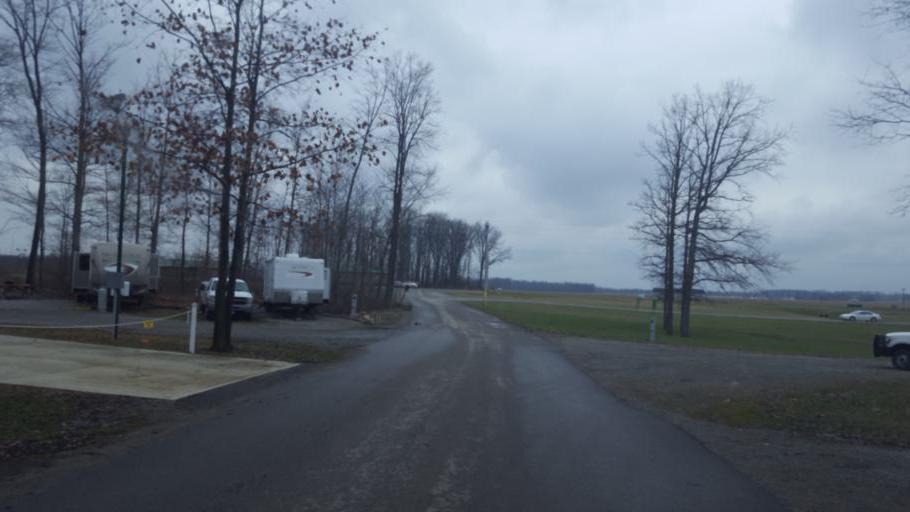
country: US
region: Ohio
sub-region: Delaware County
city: Ashley
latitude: 40.3714
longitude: -82.8391
